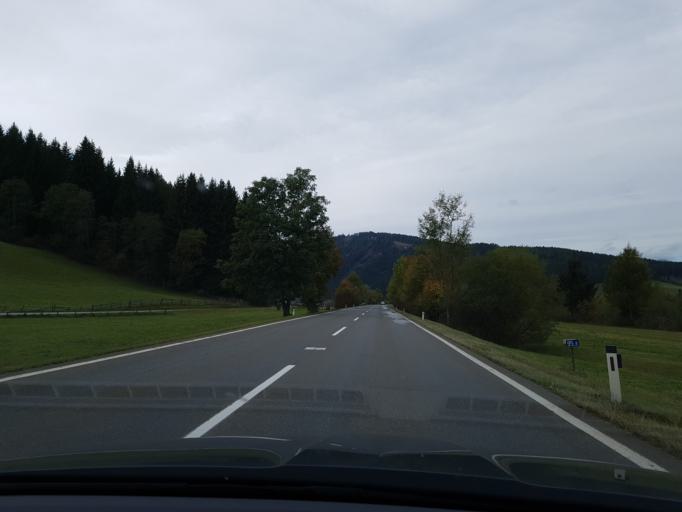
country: AT
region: Salzburg
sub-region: Politischer Bezirk Tamsweg
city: Tamsweg
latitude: 47.1255
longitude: 13.8022
